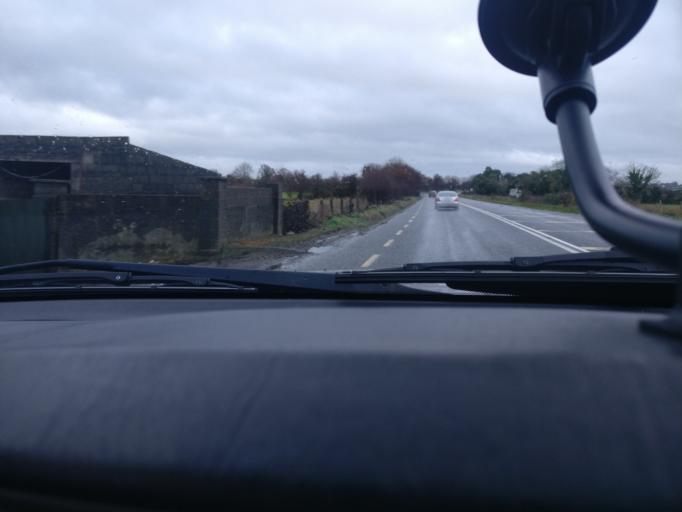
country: IE
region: Leinster
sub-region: An Mhi
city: Enfield
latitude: 53.4143
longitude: -6.8105
